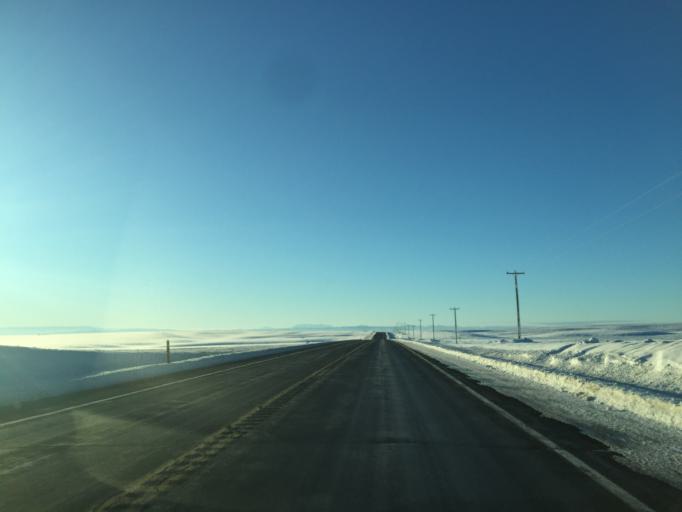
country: US
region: Washington
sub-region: Grant County
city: Soap Lake
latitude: 47.5994
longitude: -119.5600
